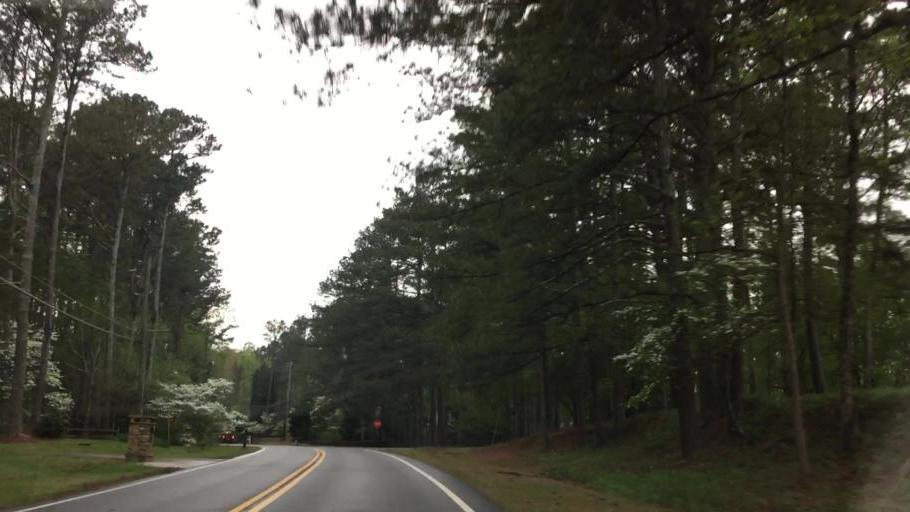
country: US
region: Georgia
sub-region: Fulton County
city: Milton
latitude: 34.1727
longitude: -84.2950
